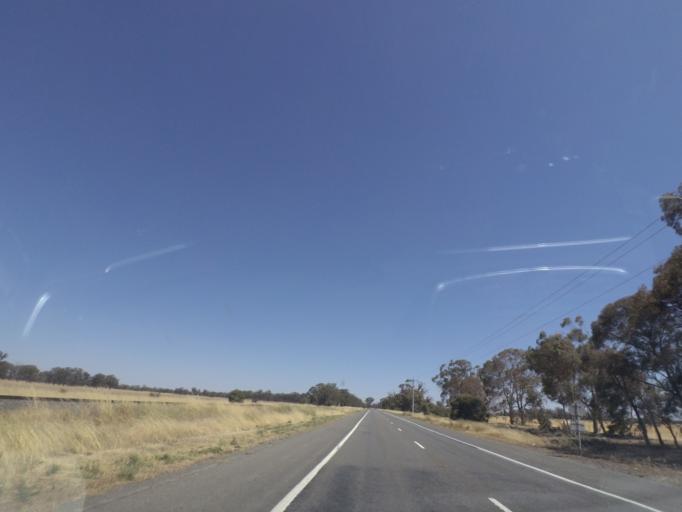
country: AU
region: Victoria
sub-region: Greater Shepparton
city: Shepparton
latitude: -36.2203
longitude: 145.4318
